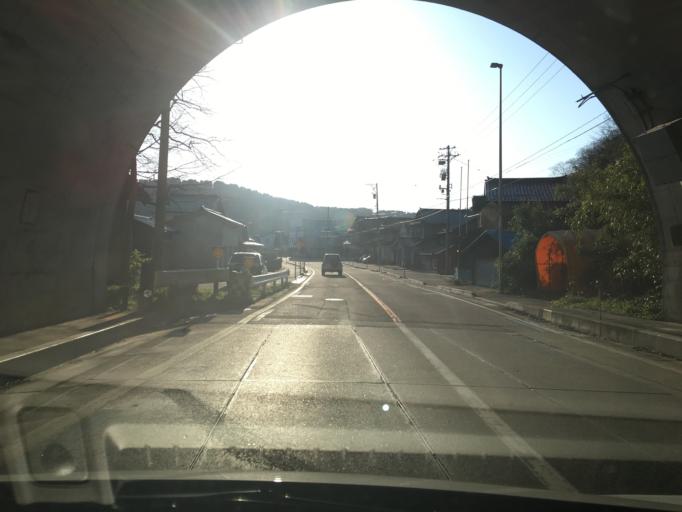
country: JP
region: Toyama
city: Himi
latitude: 36.9133
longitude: 137.0231
